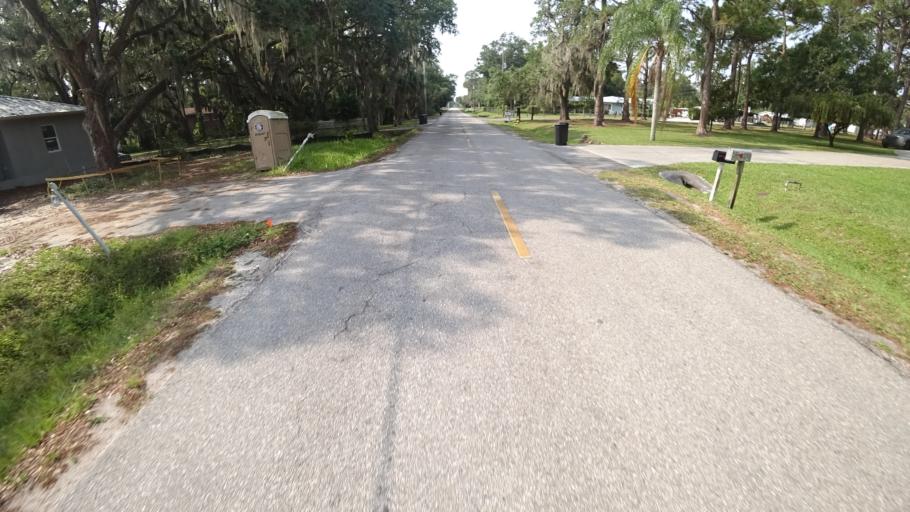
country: US
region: Florida
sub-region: Manatee County
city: Samoset
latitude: 27.4734
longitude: -82.4976
